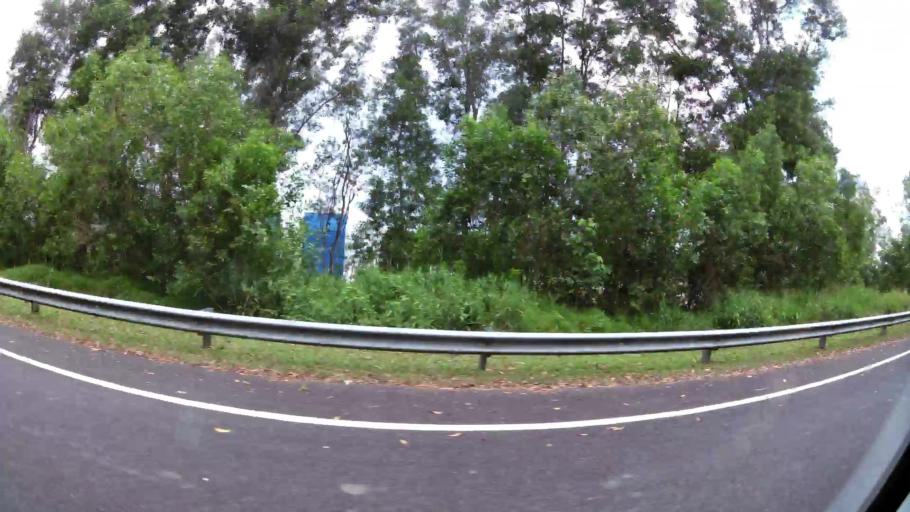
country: BN
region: Brunei and Muara
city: Bandar Seri Begawan
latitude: 4.9566
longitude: 114.8997
